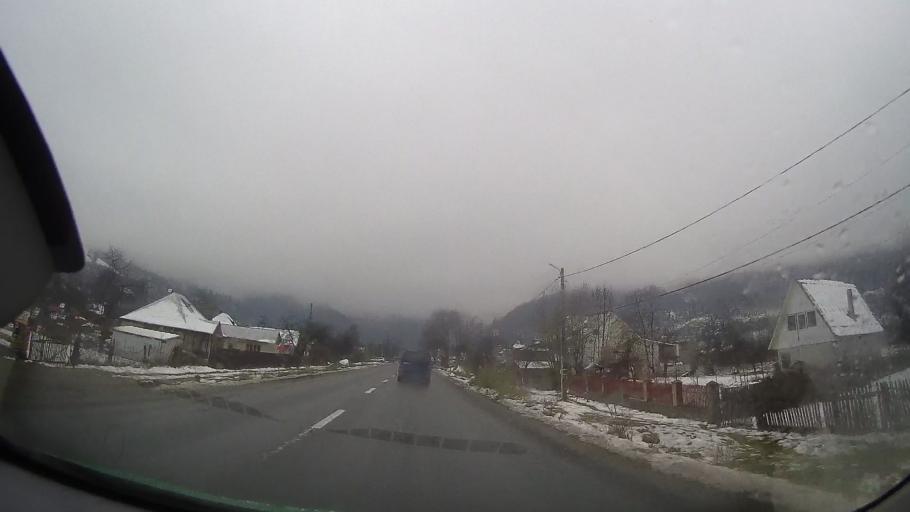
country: RO
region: Neamt
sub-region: Comuna Pangarati
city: Stejaru
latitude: 46.9026
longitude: 26.1742
